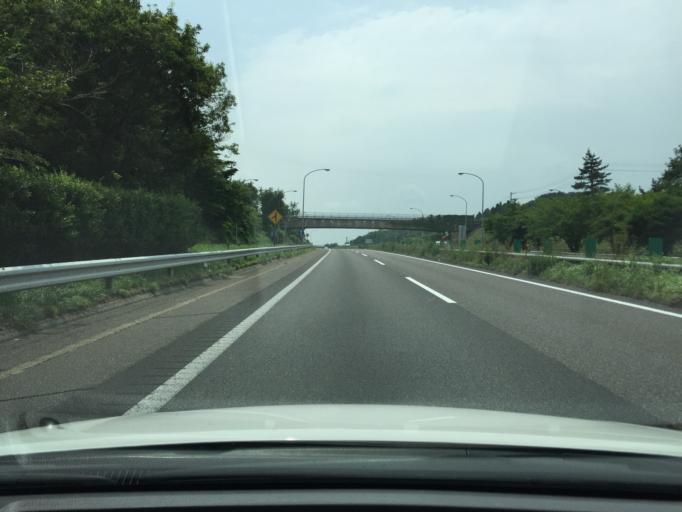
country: JP
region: Fukushima
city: Motomiya
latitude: 37.5149
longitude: 140.3813
